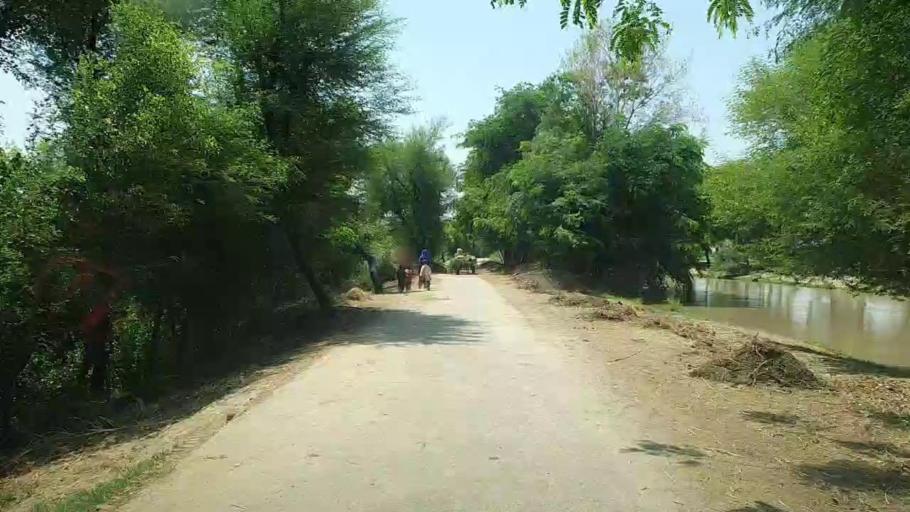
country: PK
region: Sindh
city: Ubauro
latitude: 28.1455
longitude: 69.7762
